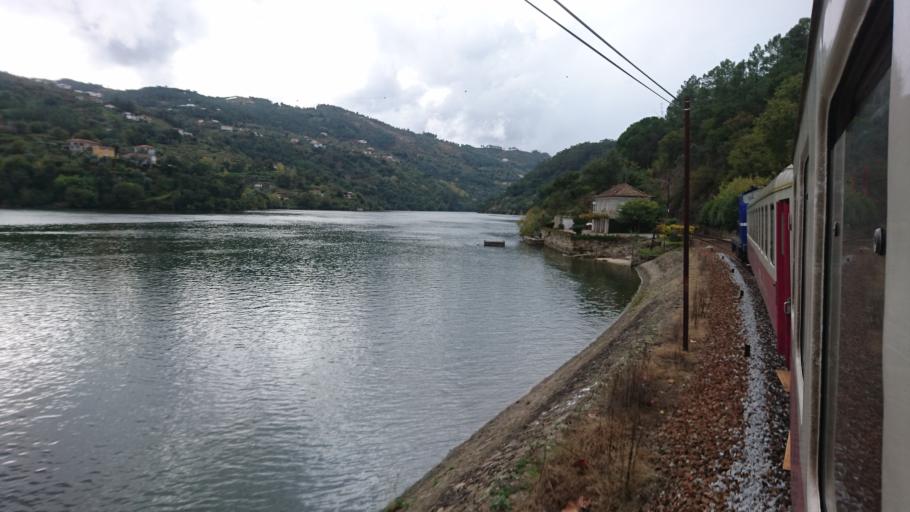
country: PT
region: Viseu
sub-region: Cinfaes
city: Cinfaes
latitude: 41.0966
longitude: -8.0375
